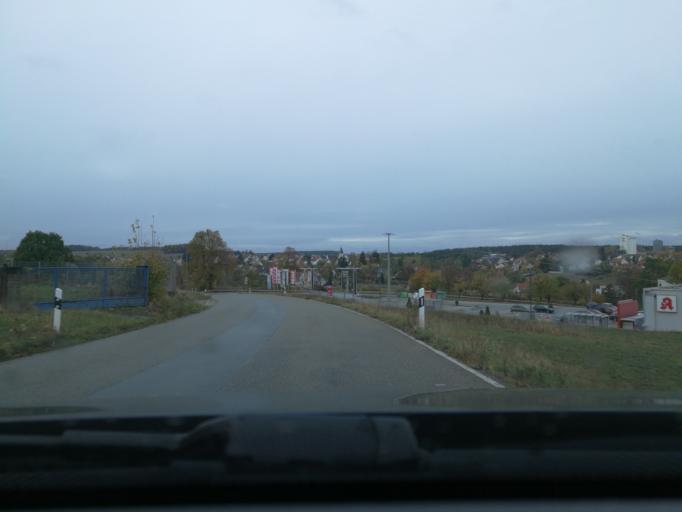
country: DE
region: Bavaria
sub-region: Regierungsbezirk Mittelfranken
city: Emskirchen
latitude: 49.5474
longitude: 10.7174
